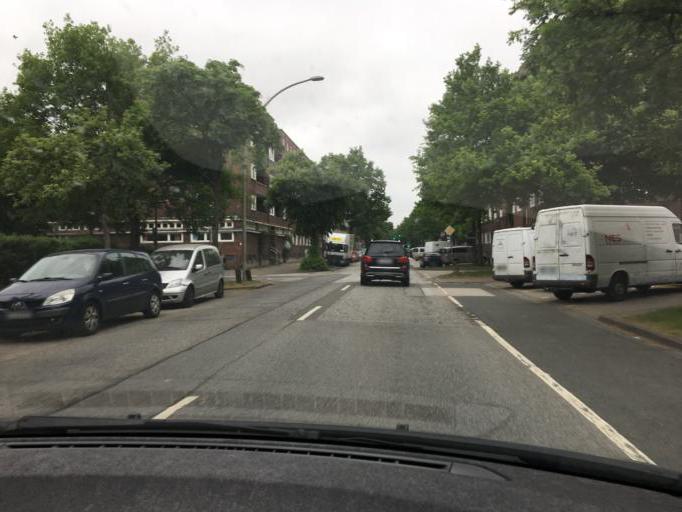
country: DE
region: Hamburg
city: Kleiner Grasbrook
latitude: 53.5136
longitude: 9.9931
